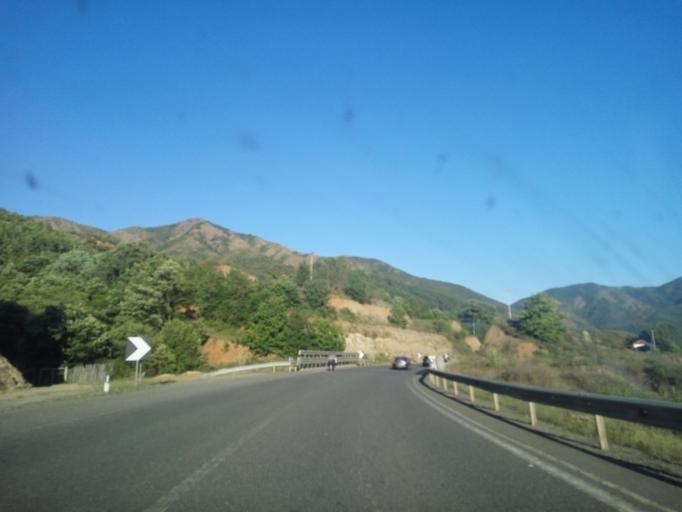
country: AL
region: Lezhe
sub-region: Rrethi i Mirdites
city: Rubik
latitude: 41.7926
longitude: 19.8128
